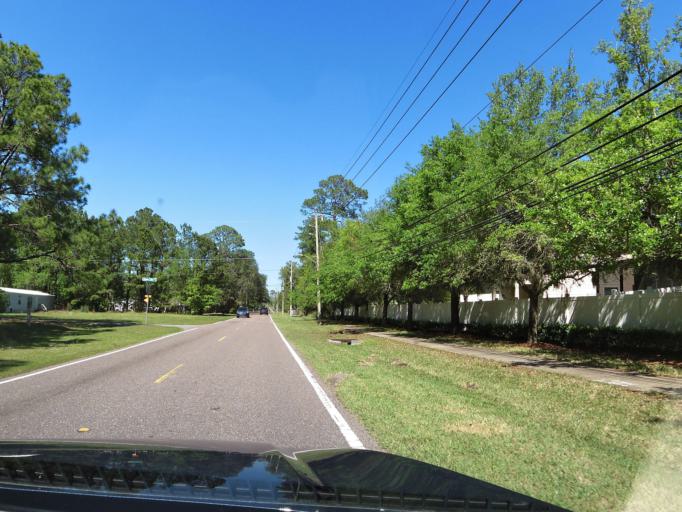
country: US
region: Florida
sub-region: Duval County
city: Jacksonville
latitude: 30.4580
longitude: -81.5941
